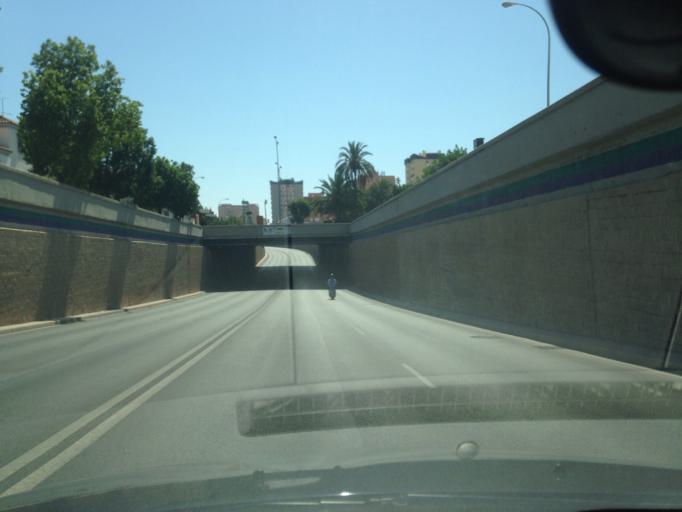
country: ES
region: Andalusia
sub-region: Provincia de Malaga
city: Malaga
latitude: 36.7160
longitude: -4.4484
